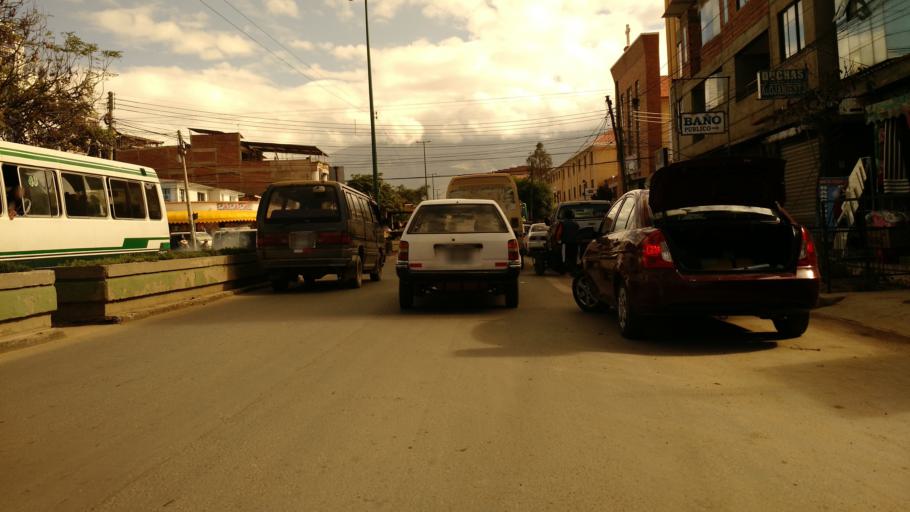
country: BO
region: Cochabamba
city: Cochabamba
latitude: -17.4081
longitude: -66.1508
